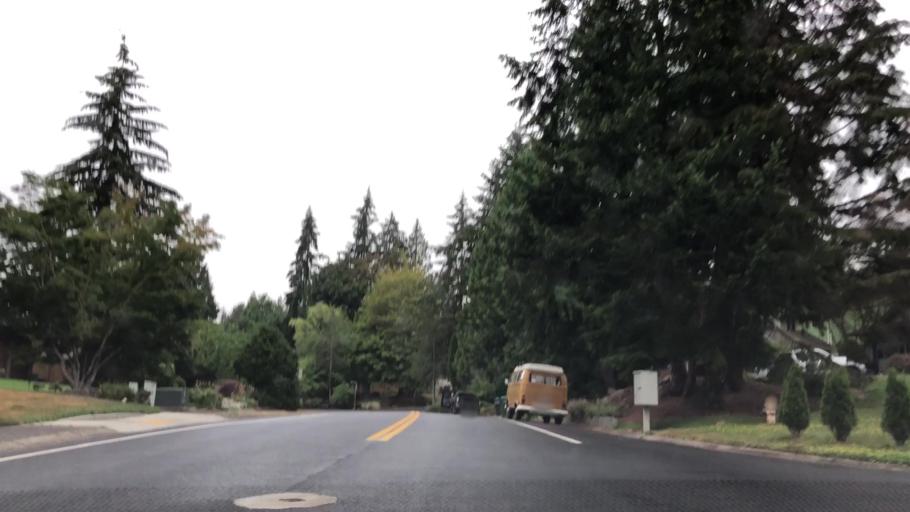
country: US
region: Washington
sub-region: Snohomish County
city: North Creek
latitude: 47.8277
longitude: -122.1996
